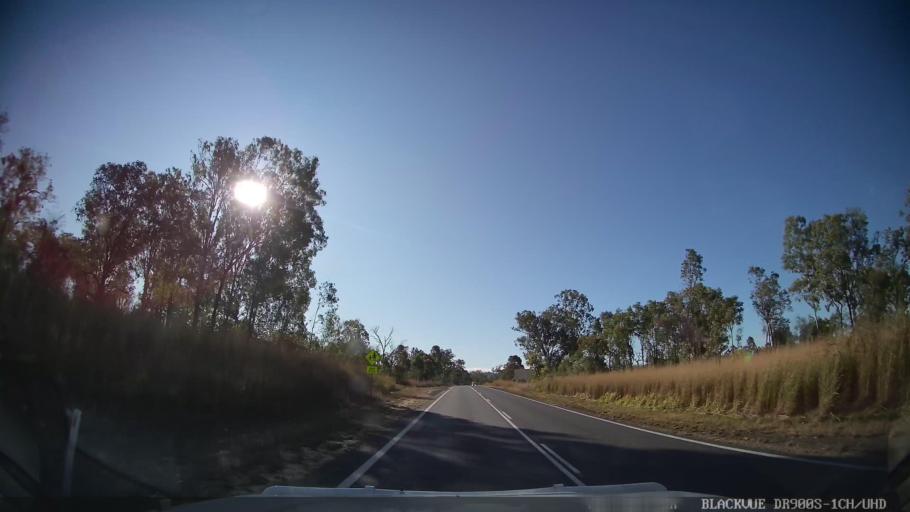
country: AU
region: Queensland
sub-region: Bundaberg
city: Sharon
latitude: -24.8258
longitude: 151.7069
